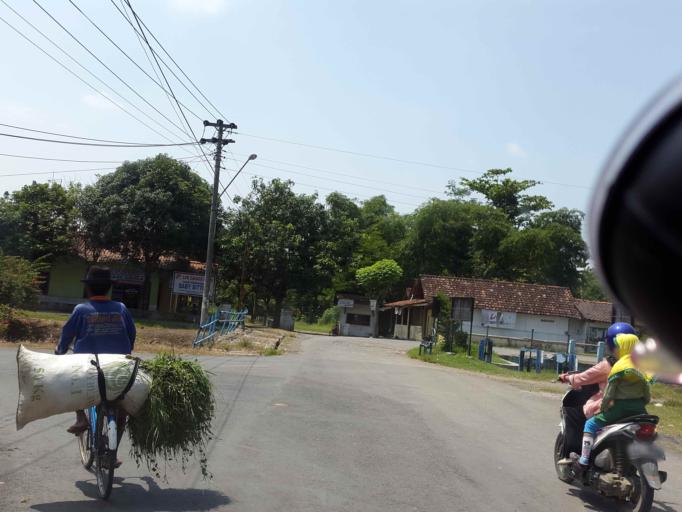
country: ID
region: Central Java
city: Petarukan
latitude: -6.9447
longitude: 109.4680
